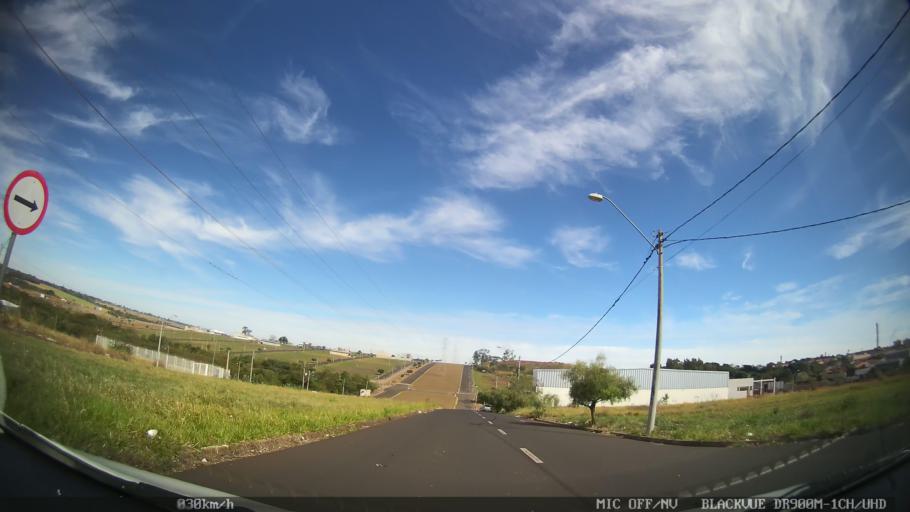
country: BR
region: Sao Paulo
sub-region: Sao Jose Do Rio Preto
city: Sao Jose do Rio Preto
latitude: -20.8469
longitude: -49.3728
